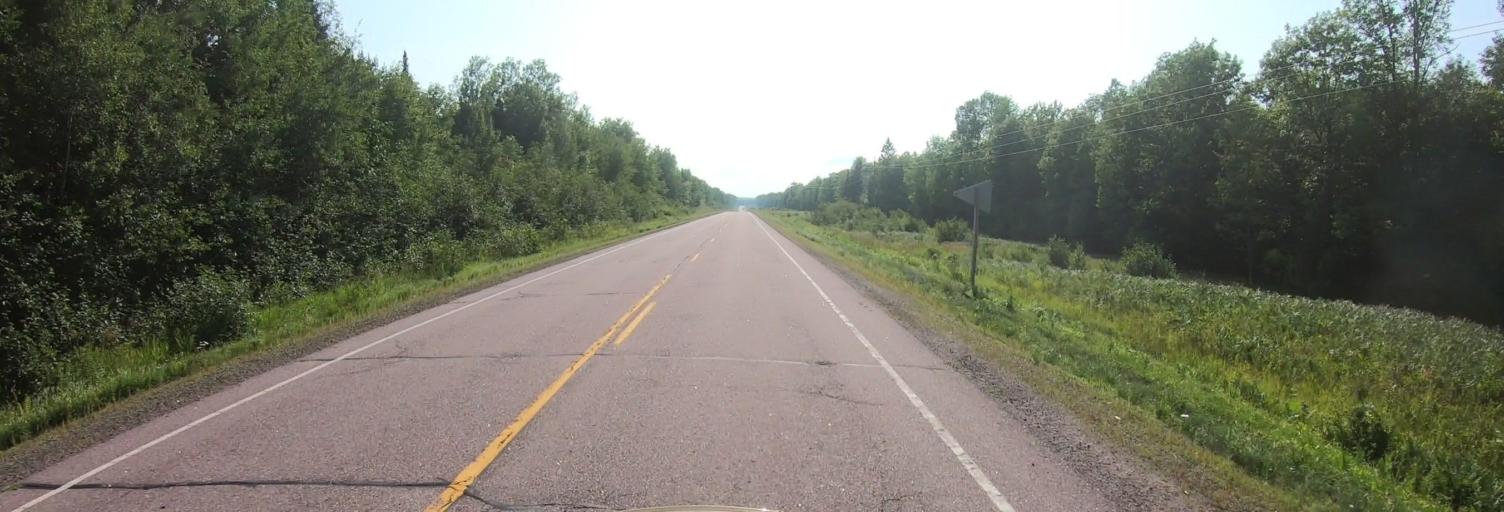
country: US
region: Wisconsin
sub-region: Iron County
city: Hurley
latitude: 46.3599
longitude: -90.4526
